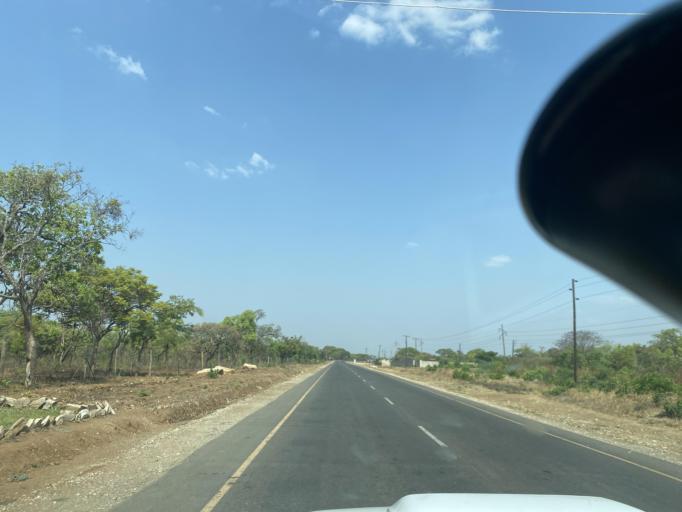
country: ZM
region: Lusaka
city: Lusaka
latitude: -15.3454
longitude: 28.0922
